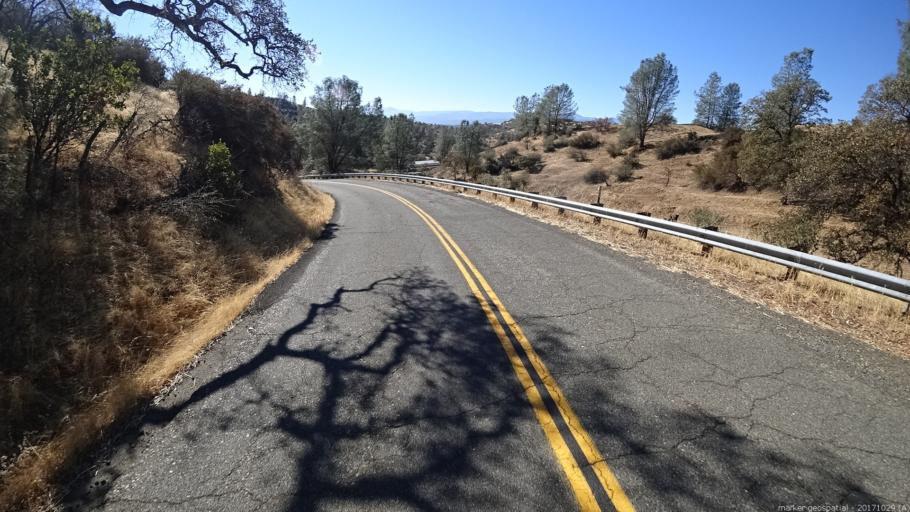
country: US
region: California
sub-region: Trinity County
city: Lewiston
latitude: 40.4202
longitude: -122.7666
